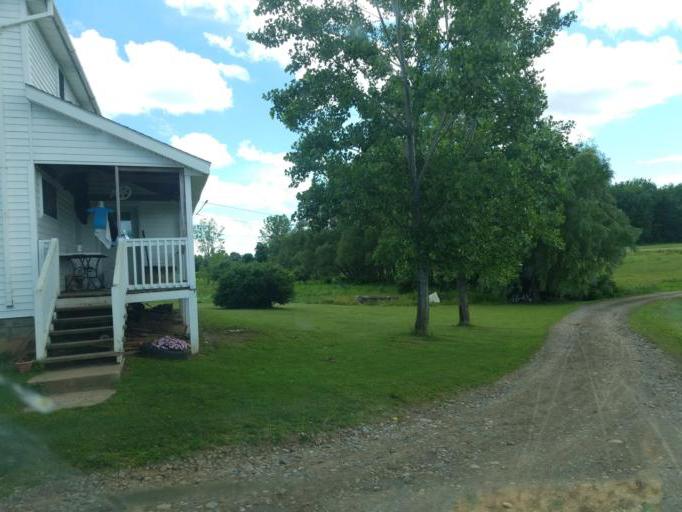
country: US
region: New York
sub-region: Wayne County
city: Clyde
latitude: 43.0515
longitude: -76.8827
